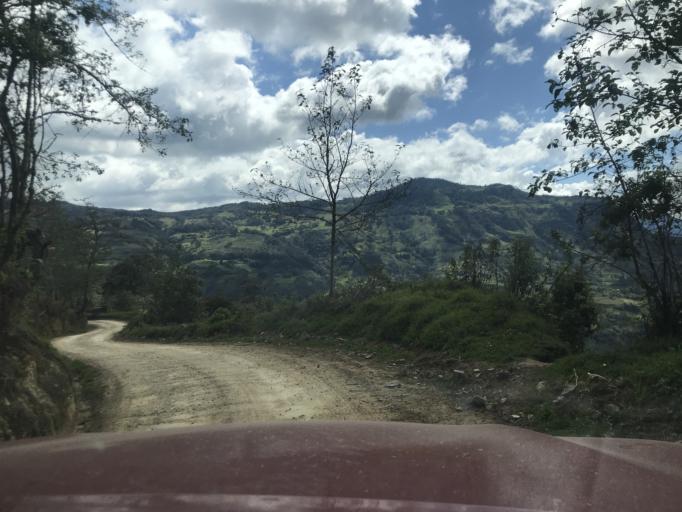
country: PE
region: Cajamarca
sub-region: Provincia de Chota
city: Querocoto
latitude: -6.3426
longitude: -79.0490
